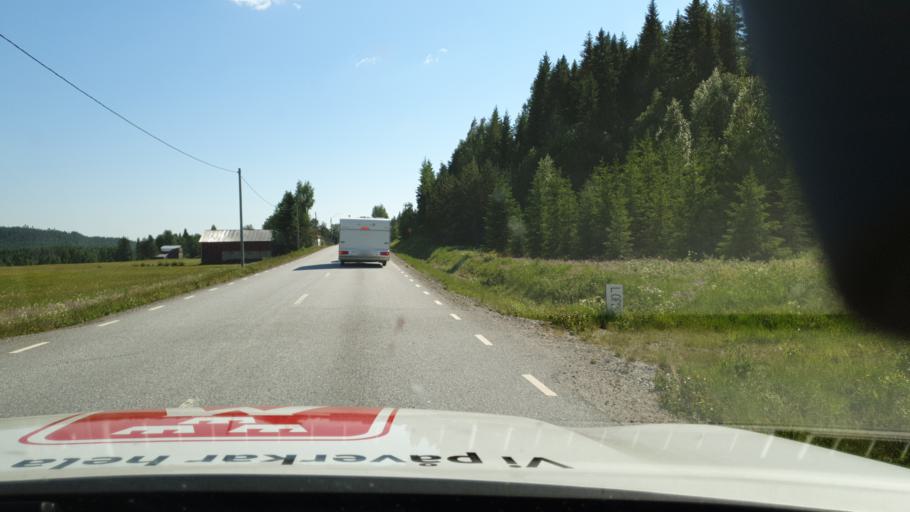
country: SE
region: Vaesterbotten
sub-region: Umea Kommun
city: Ersmark
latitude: 64.3117
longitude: 20.2221
